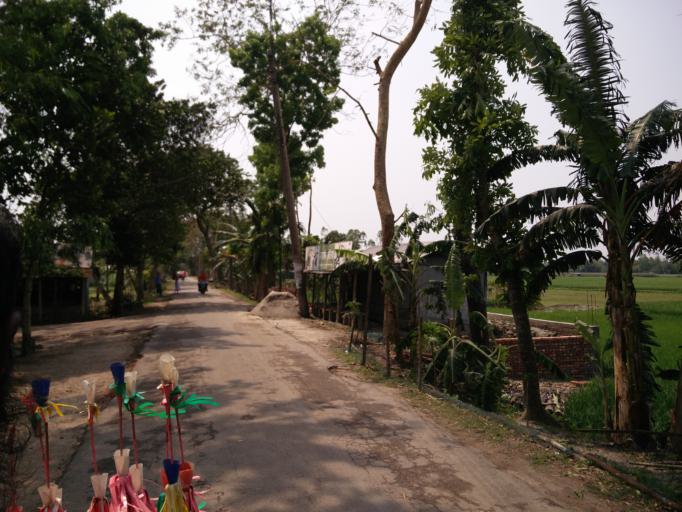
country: BD
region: Dhaka
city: Sherpur
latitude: 24.9531
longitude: 90.1662
